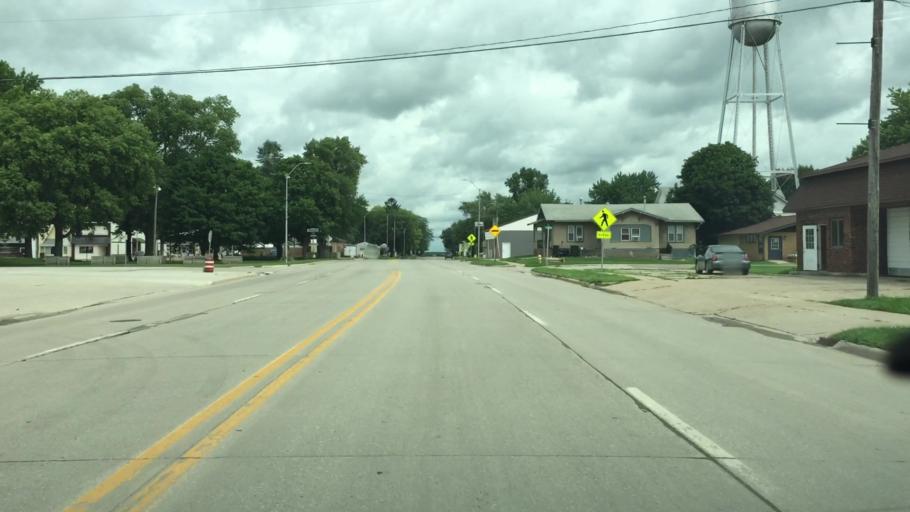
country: US
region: Iowa
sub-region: Jasper County
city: Monroe
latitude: 41.5210
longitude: -93.1018
